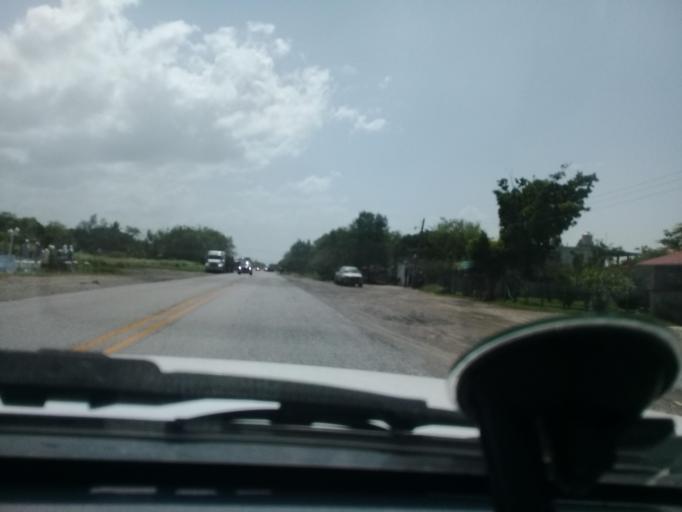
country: MX
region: Veracruz
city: Moralillo
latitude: 22.1715
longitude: -98.0473
